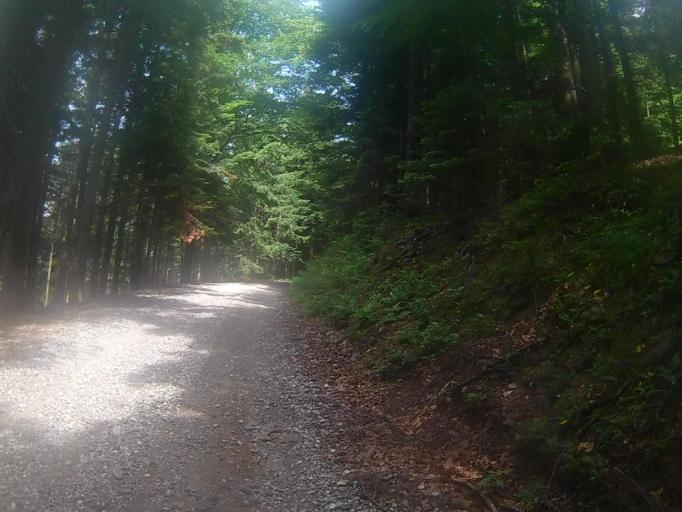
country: SI
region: Ruse
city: Bistrica ob Dravi
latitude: 46.5158
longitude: 15.5534
